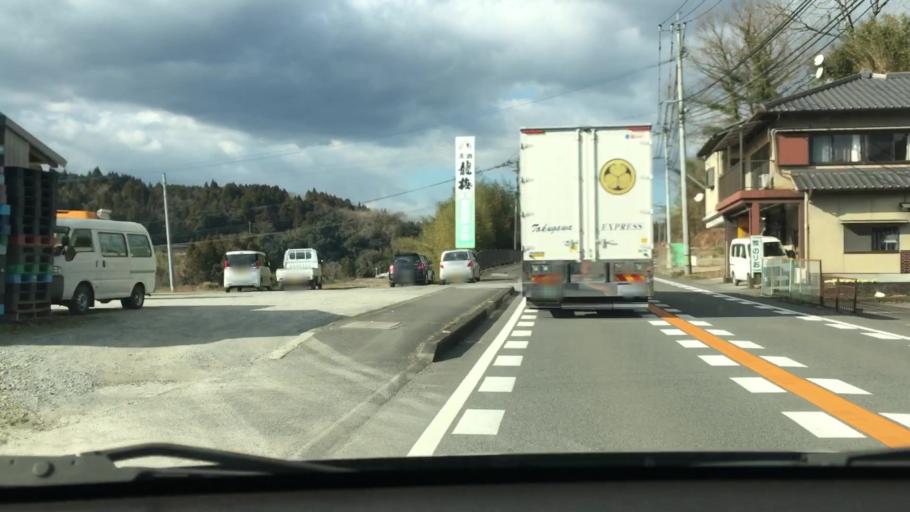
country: JP
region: Oita
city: Usuki
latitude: 33.0495
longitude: 131.6895
